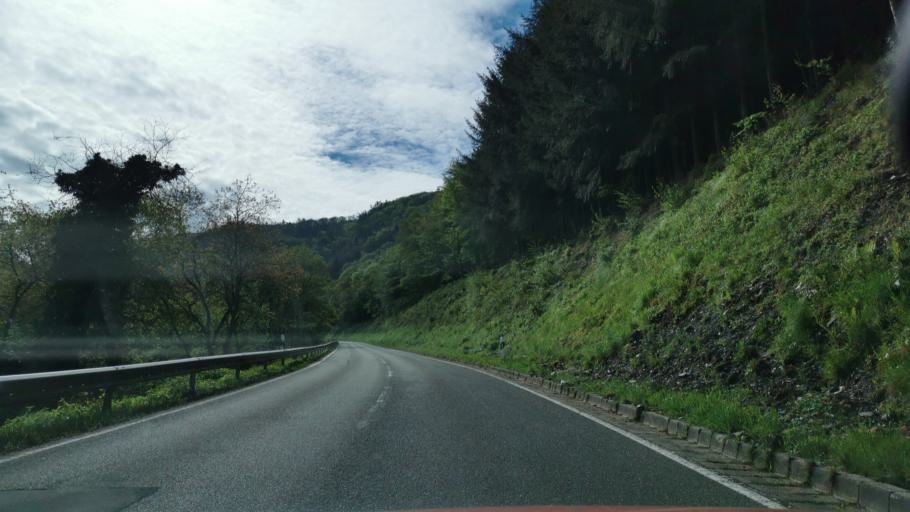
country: DE
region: Rheinland-Pfalz
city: Traben-Trarbach
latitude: 49.9410
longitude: 7.1159
